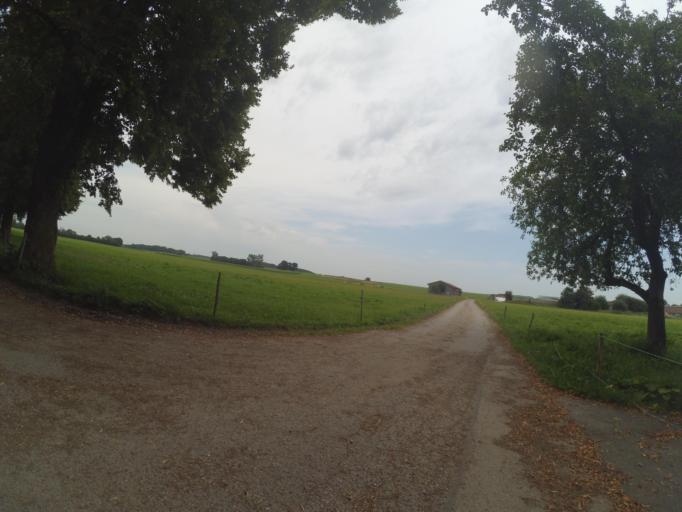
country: DE
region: Bavaria
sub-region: Swabia
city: Jengen
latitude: 48.0060
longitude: 10.7250
